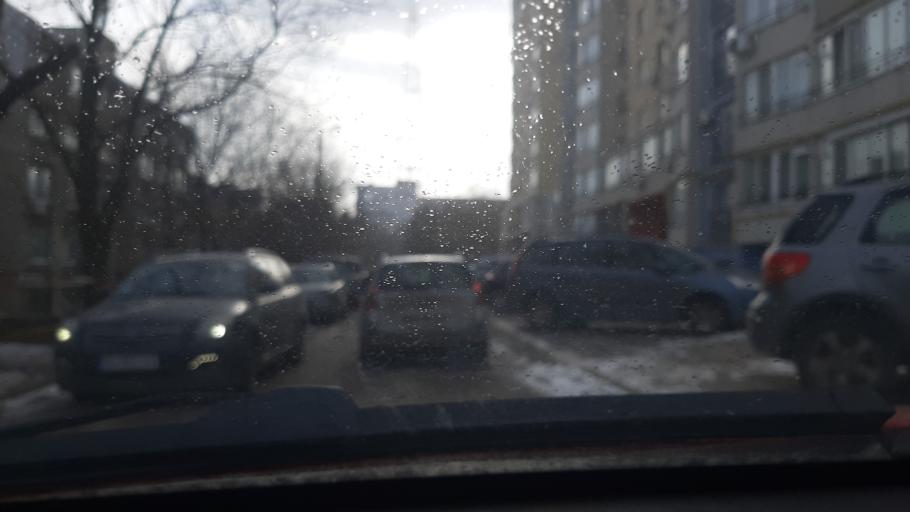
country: MD
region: Chisinau
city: Chisinau
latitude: 47.0034
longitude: 28.8066
